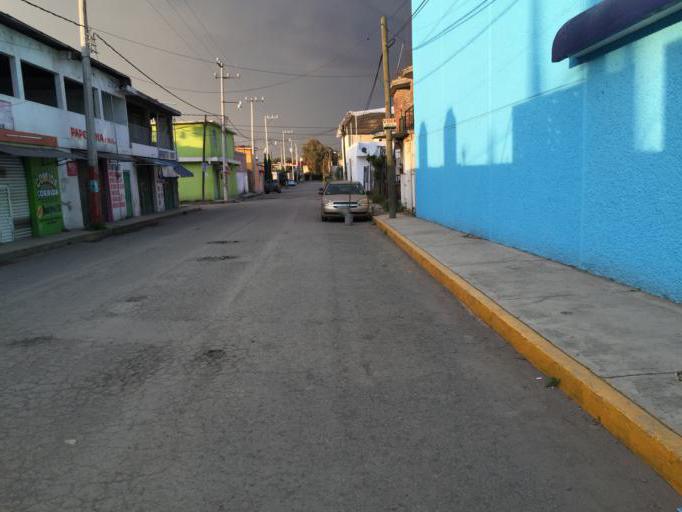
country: MX
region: Mexico
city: Cuautitlan Izcalli
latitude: 19.6662
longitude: -99.2198
